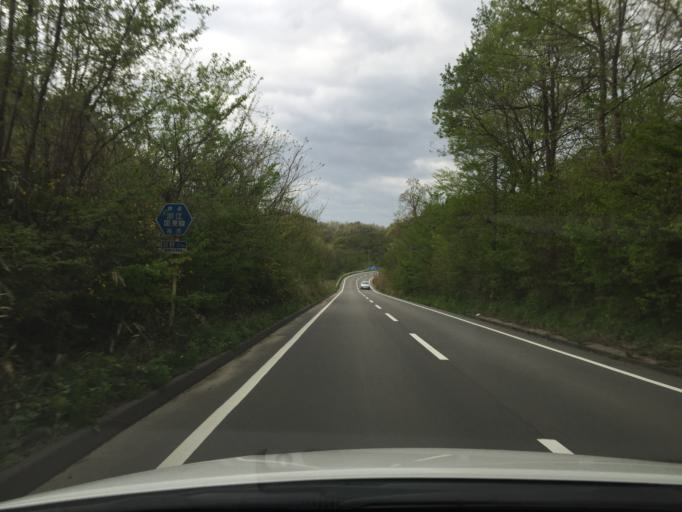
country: JP
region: Fukushima
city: Yanagawamachi-saiwaicho
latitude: 37.7266
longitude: 140.7327
